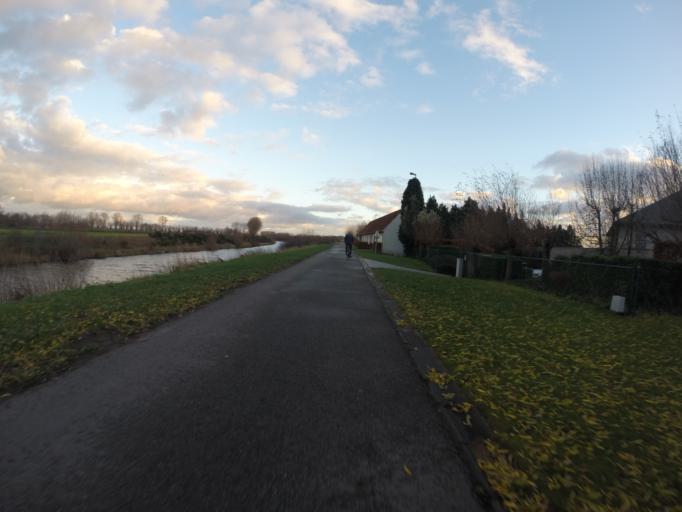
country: BE
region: Flanders
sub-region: Provincie Oost-Vlaanderen
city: Aalter
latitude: 51.1056
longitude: 3.4670
